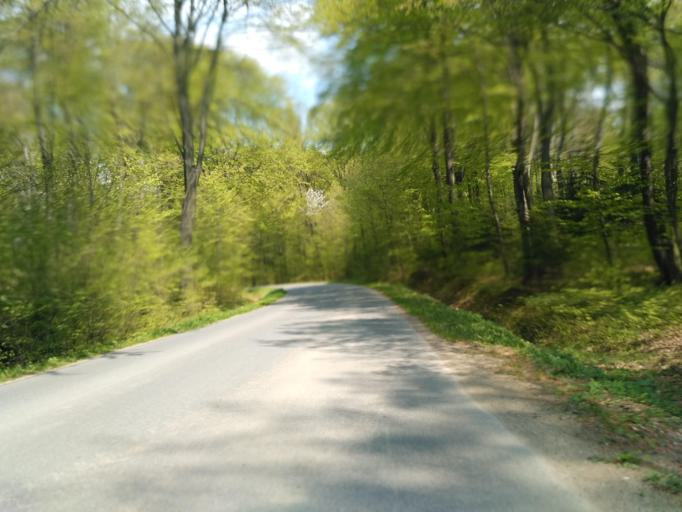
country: PL
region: Subcarpathian Voivodeship
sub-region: Powiat jasielski
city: Debowiec
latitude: 49.7041
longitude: 21.5115
